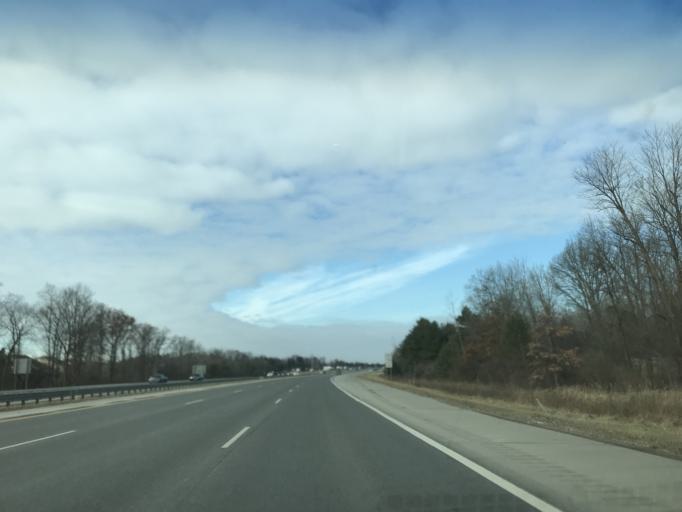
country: US
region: Michigan
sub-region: Oakland County
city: Pontiac
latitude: 42.7059
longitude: -83.3215
